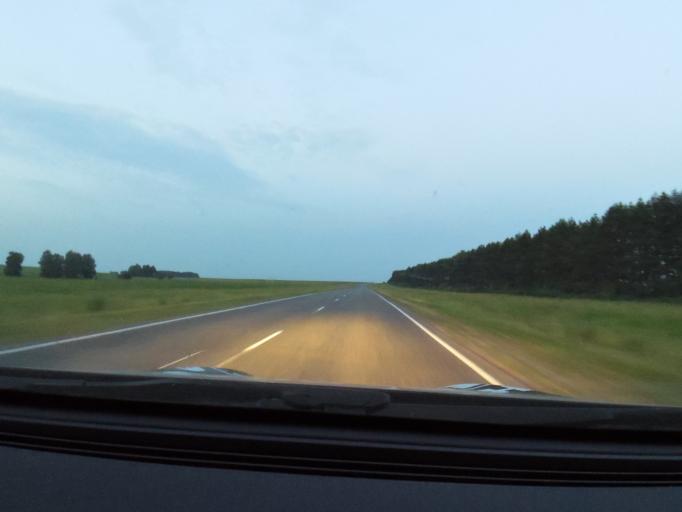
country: RU
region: Bashkortostan
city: Duvan
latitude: 56.1209
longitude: 58.0335
